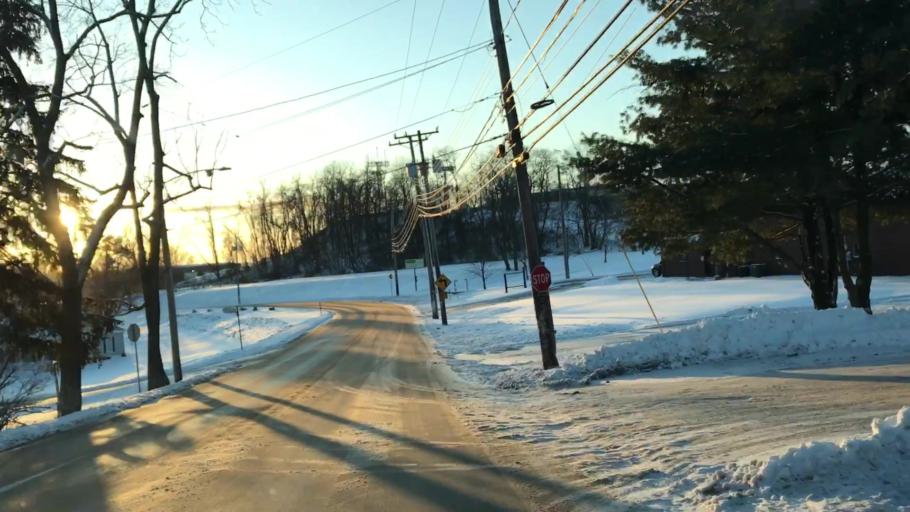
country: US
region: Pennsylvania
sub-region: Allegheny County
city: Carnot-Moon
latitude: 40.5107
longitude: -80.2452
